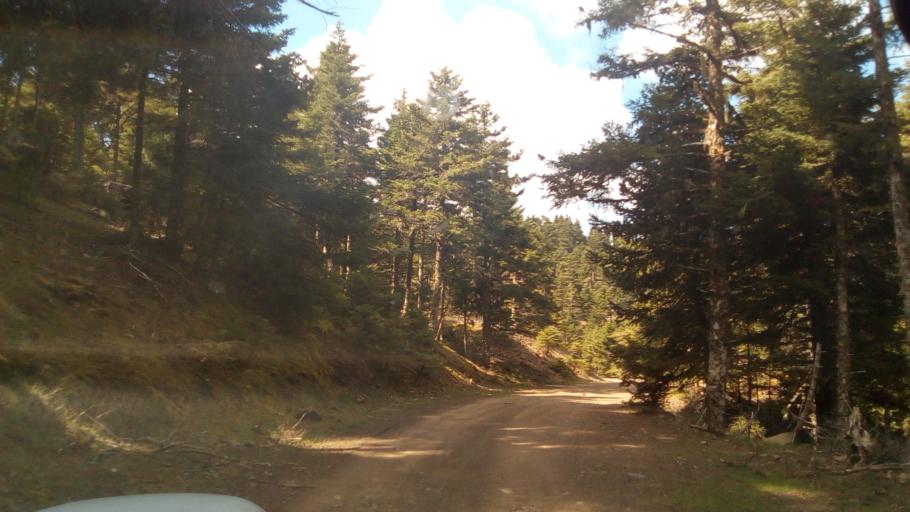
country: GR
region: West Greece
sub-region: Nomos Aitolias kai Akarnanias
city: Nafpaktos
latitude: 38.6390
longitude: 21.9438
